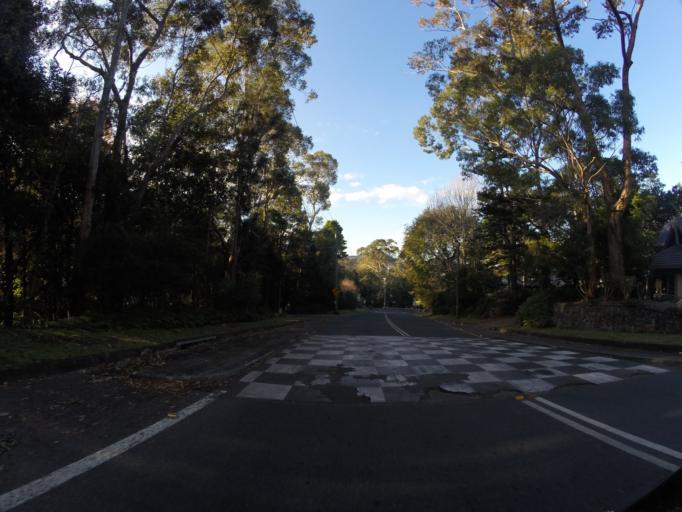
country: AU
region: New South Wales
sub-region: Wollongong
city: Cordeaux Heights
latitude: -34.4318
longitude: 150.8158
